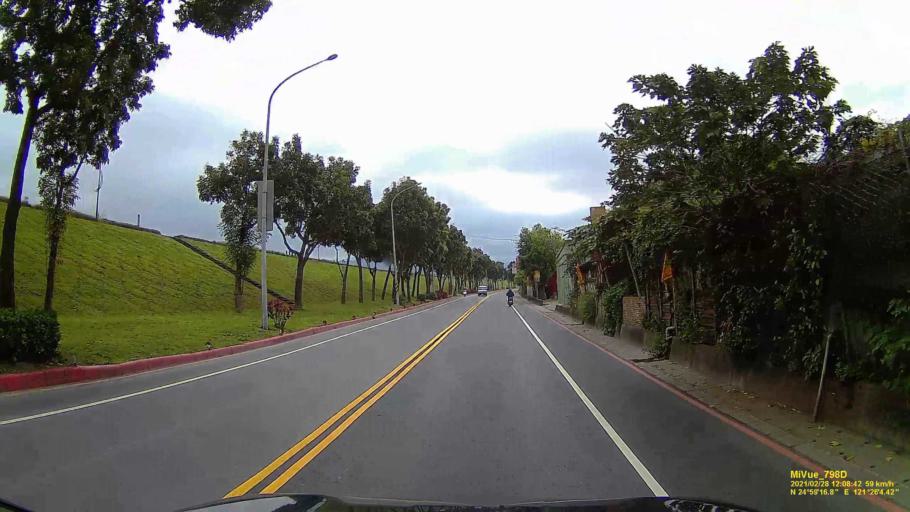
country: TW
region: Taipei
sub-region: Taipei
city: Banqiao
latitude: 24.9877
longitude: 121.4345
